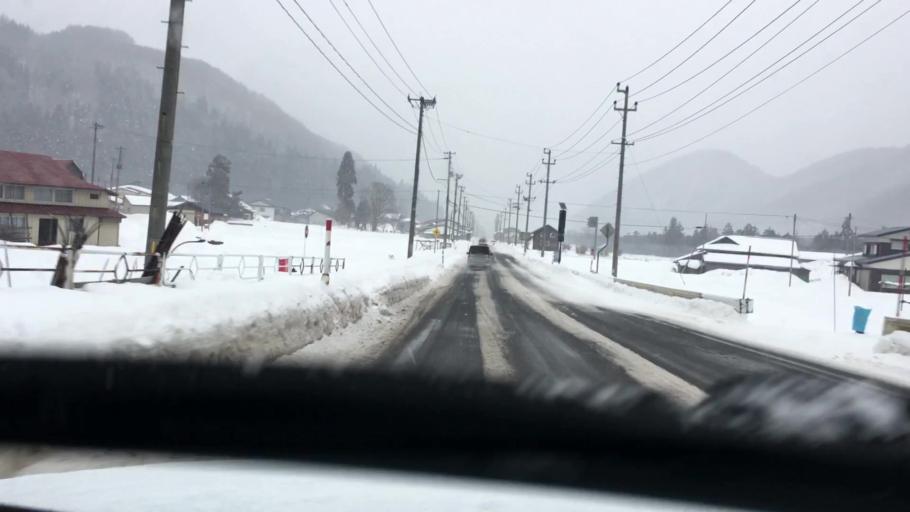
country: JP
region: Akita
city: Hanawa
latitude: 40.0662
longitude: 141.0158
